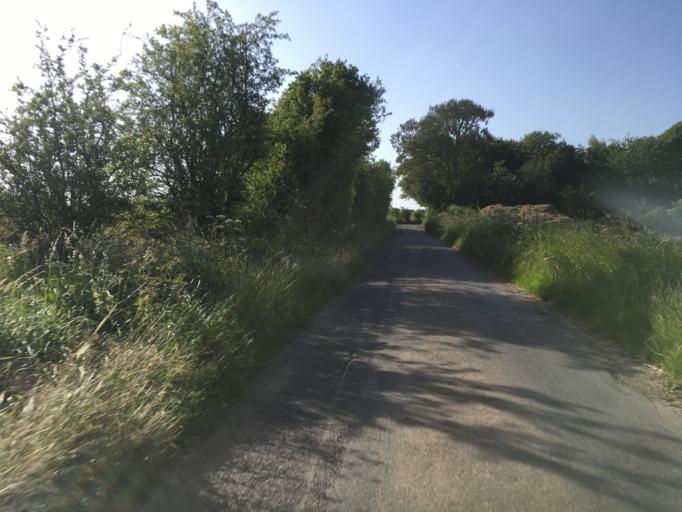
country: GB
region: England
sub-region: Oxfordshire
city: Burford
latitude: 51.7771
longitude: -1.7028
